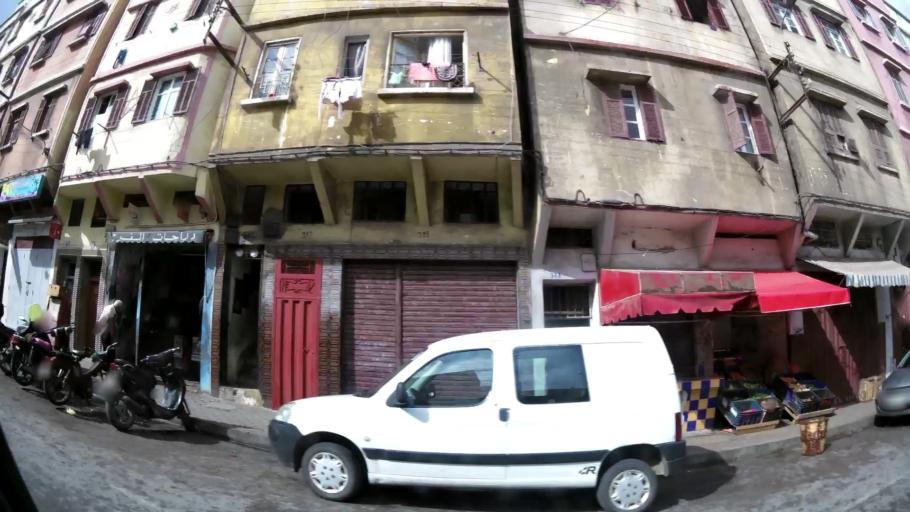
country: MA
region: Grand Casablanca
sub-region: Casablanca
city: Casablanca
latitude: 33.5709
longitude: -7.5868
